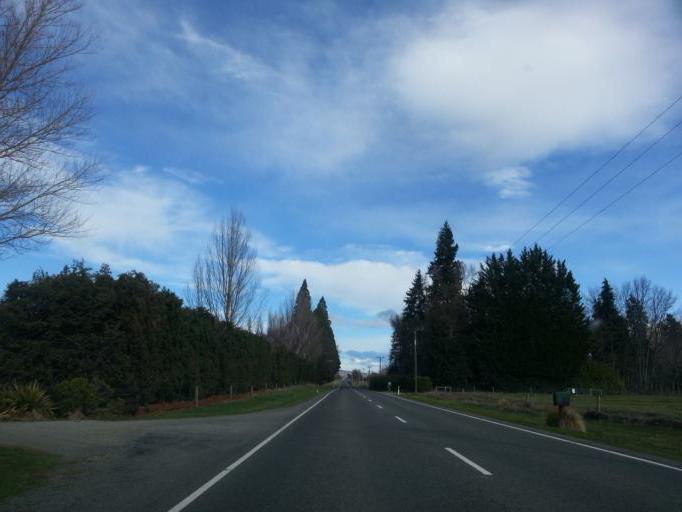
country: NZ
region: Canterbury
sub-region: Hurunui District
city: Amberley
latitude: -42.7908
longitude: 172.8346
